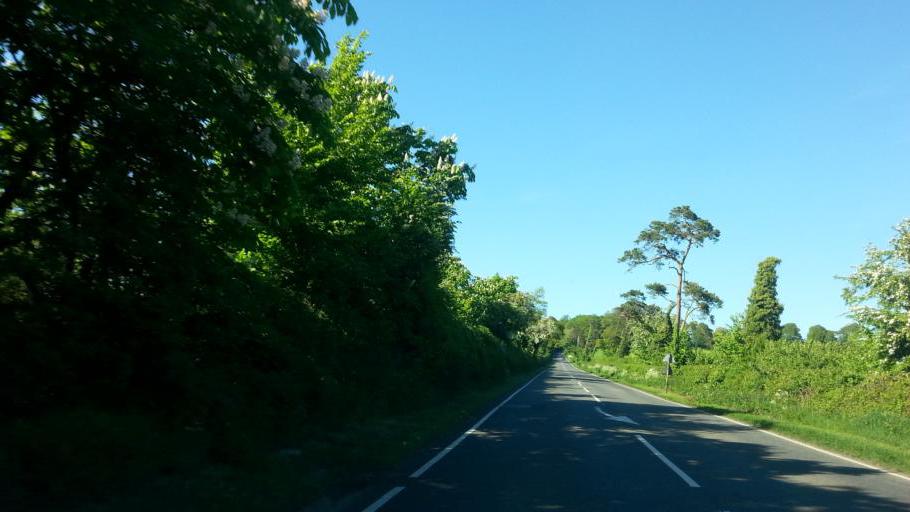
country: GB
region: England
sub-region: Somerset
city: Milborne Port
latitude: 50.9642
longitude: -2.4287
